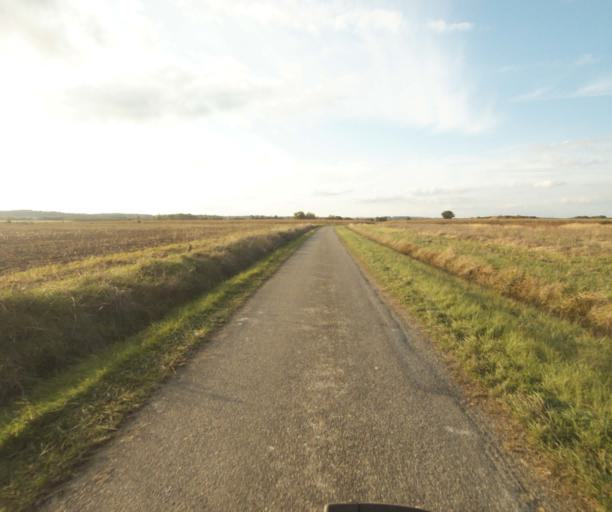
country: FR
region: Midi-Pyrenees
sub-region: Departement du Tarn-et-Garonne
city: Verdun-sur-Garonne
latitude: 43.8245
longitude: 1.1563
